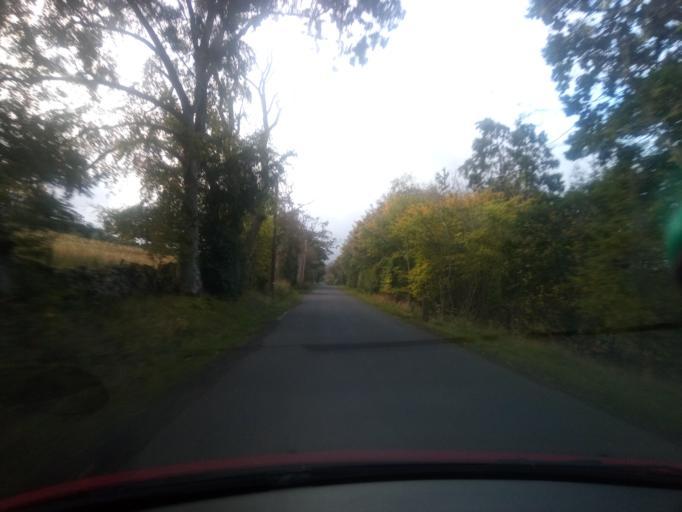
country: GB
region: Scotland
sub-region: The Scottish Borders
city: Jedburgh
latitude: 55.3725
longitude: -2.6485
